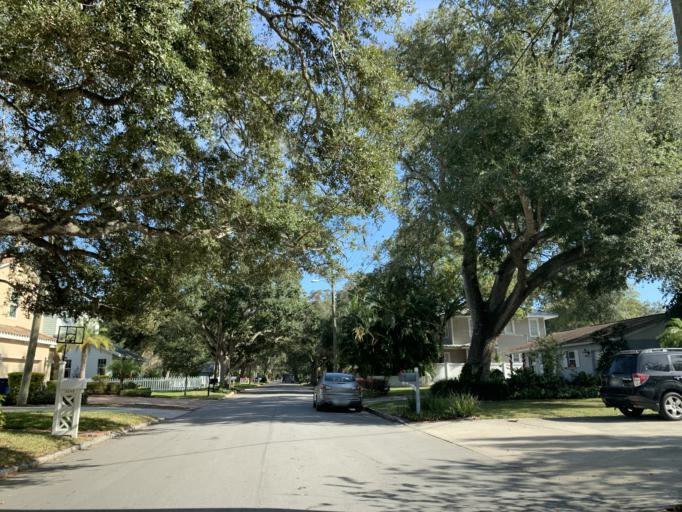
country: US
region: Florida
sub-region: Hillsborough County
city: Tampa
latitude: 27.8948
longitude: -82.4973
